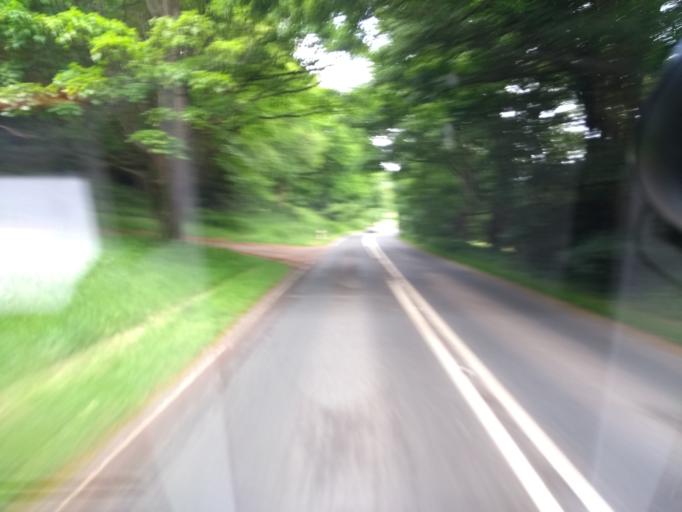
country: GB
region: England
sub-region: Somerset
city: Bishops Lydeard
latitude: 51.1584
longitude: -3.2050
